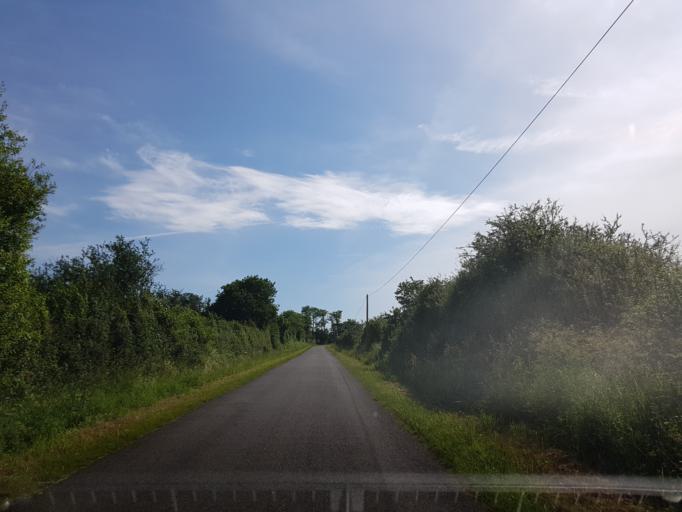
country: FR
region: Poitou-Charentes
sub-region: Departement de la Charente
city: Exideuil
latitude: 45.9158
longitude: 0.6680
